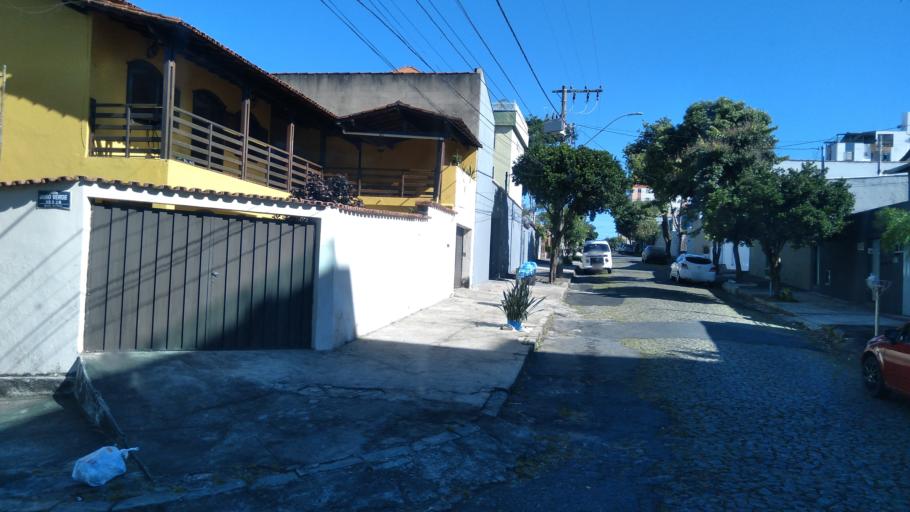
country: BR
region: Minas Gerais
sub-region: Belo Horizonte
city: Belo Horizonte
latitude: -19.8852
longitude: -43.9108
